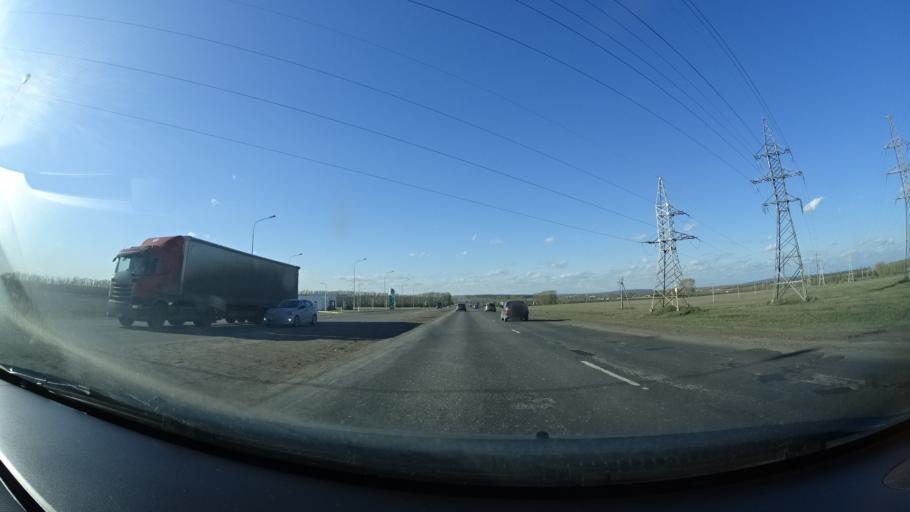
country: RU
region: Bashkortostan
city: Kabakovo
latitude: 54.4808
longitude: 55.9096
